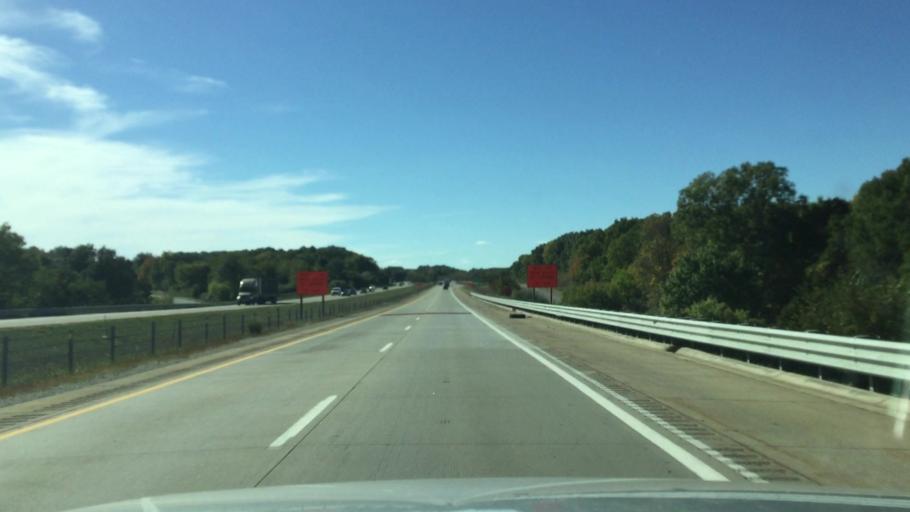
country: US
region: Michigan
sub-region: Jackson County
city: Grass Lake
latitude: 42.2921
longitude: -84.2488
